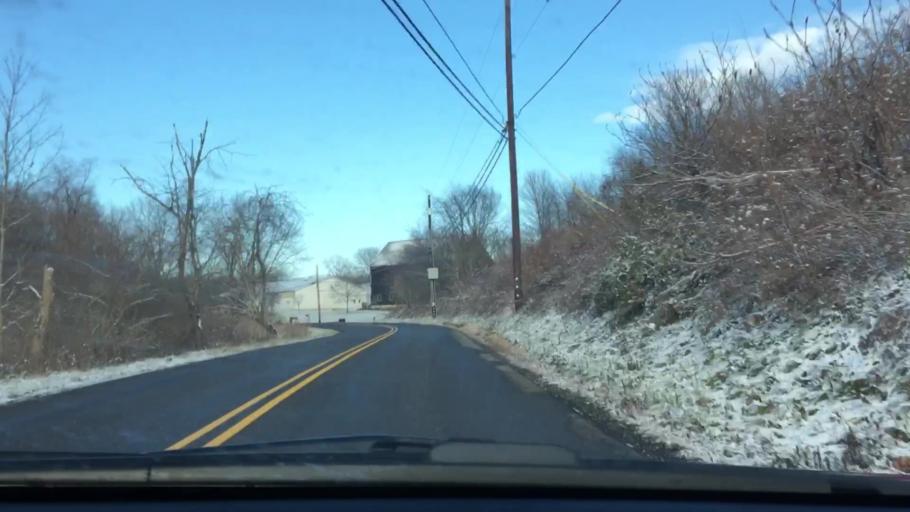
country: US
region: Pennsylvania
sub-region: Allegheny County
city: Imperial
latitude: 40.4225
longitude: -80.2344
